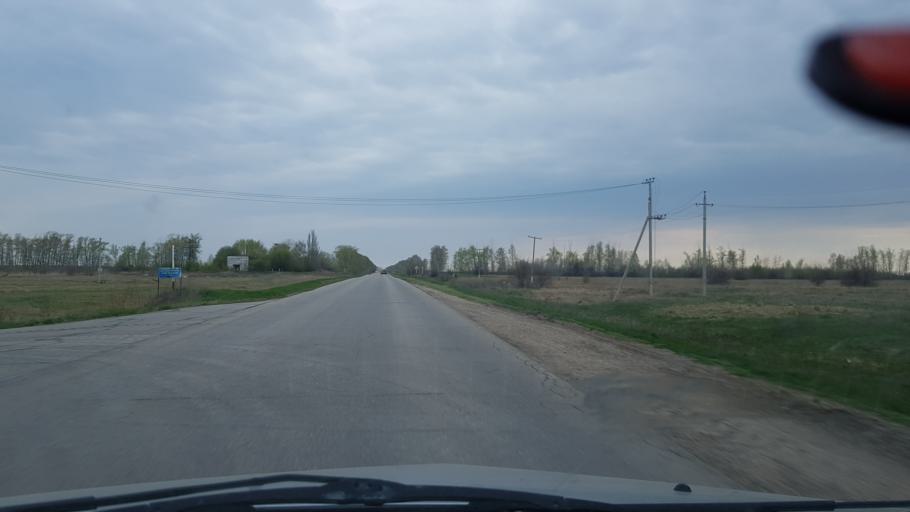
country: RU
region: Samara
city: Tol'yatti
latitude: 53.6577
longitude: 49.2474
